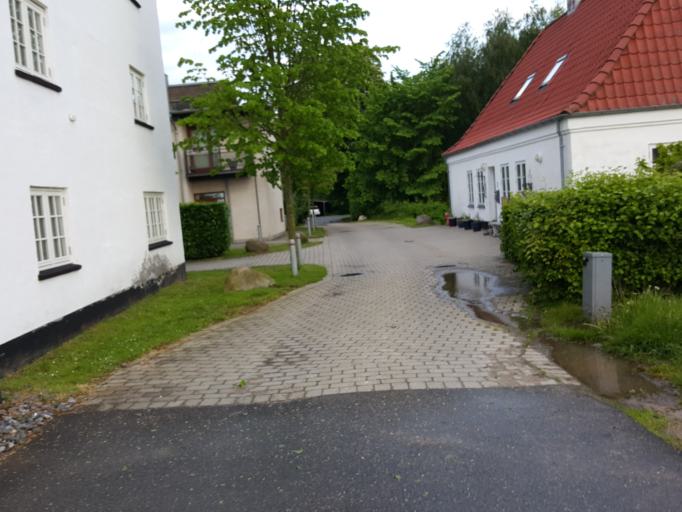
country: DK
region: Capital Region
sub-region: Rudersdal Kommune
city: Birkerod
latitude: 55.8512
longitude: 12.4565
